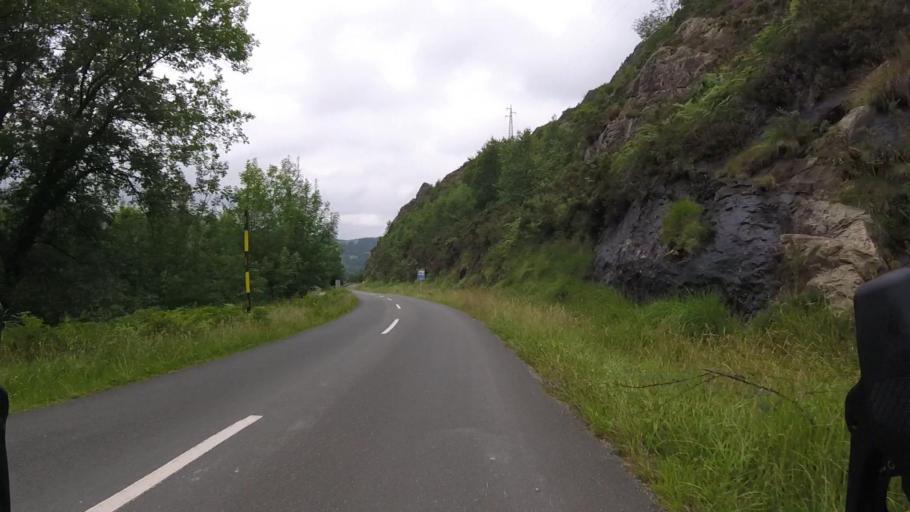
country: ES
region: Basque Country
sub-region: Provincia de Guipuzcoa
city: Irun
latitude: 43.2729
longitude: -1.7966
